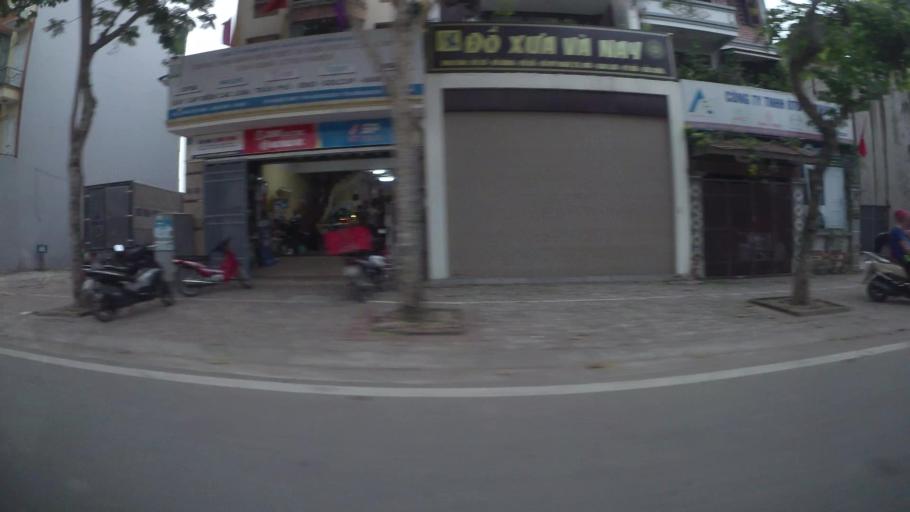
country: VN
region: Ha Noi
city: Hoan Kiem
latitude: 21.0511
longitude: 105.8964
